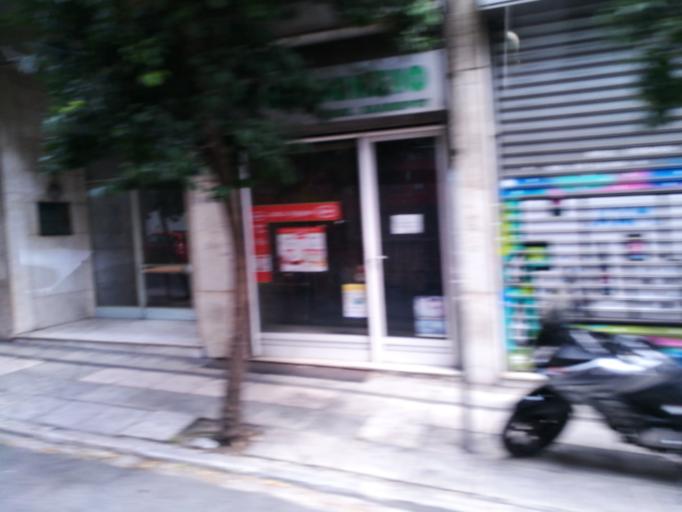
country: GR
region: Attica
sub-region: Nomarchia Athinas
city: Kipseli
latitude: 37.9899
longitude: 23.7318
